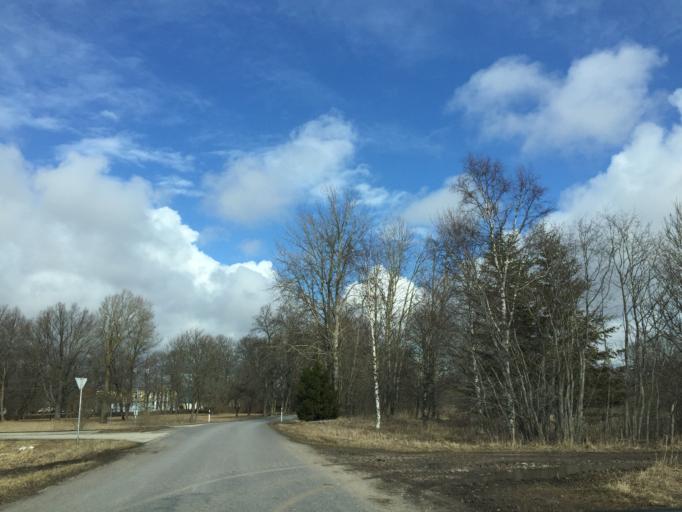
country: EE
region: Laeaene
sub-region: Lihula vald
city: Lihula
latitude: 58.7124
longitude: 23.8150
